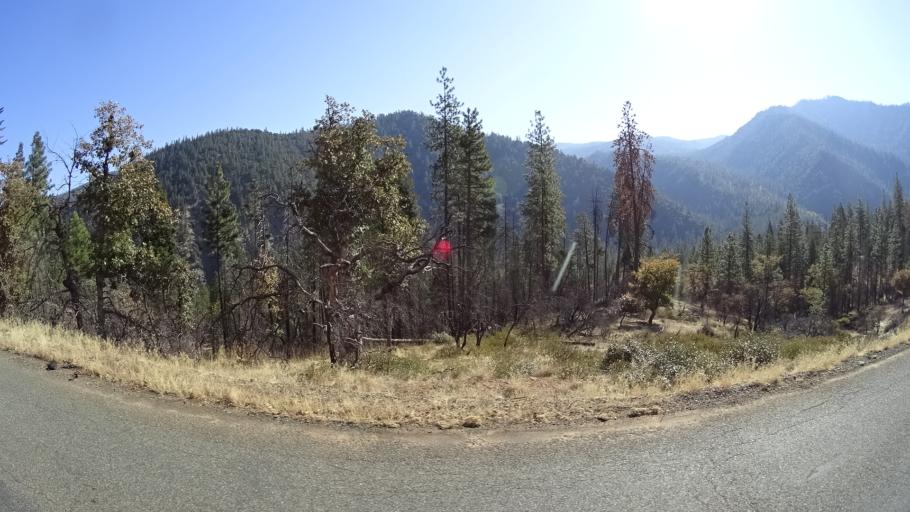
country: US
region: California
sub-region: Siskiyou County
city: Happy Camp
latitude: 41.7174
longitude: -123.0214
